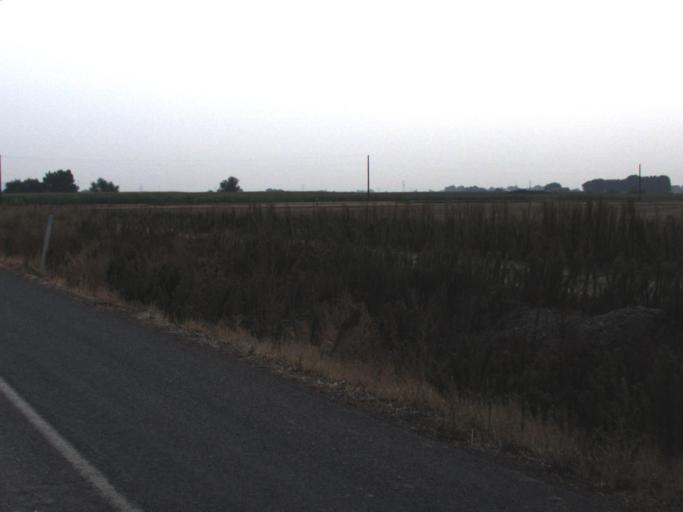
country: US
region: Washington
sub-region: Yakima County
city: Granger
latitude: 46.3284
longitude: -120.2234
